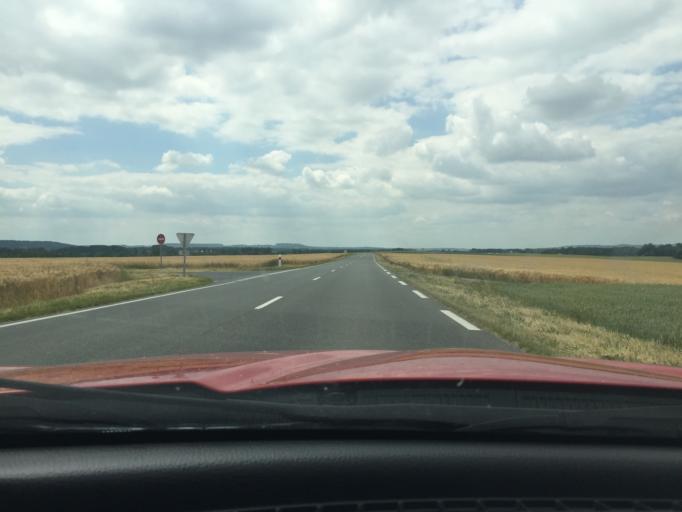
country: FR
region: Champagne-Ardenne
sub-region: Departement de la Marne
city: Cormicy
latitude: 49.4158
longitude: 3.9040
